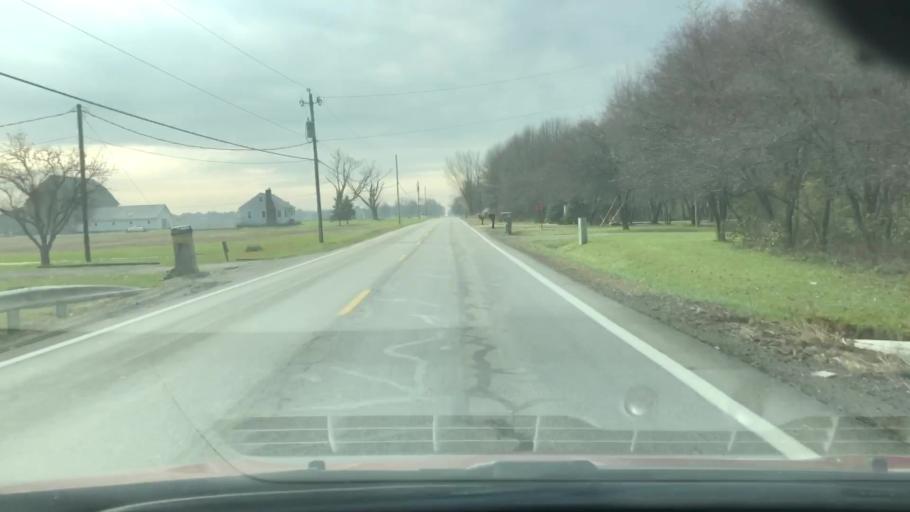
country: US
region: Ohio
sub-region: Delaware County
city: Sunbury
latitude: 40.1824
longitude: -82.8063
